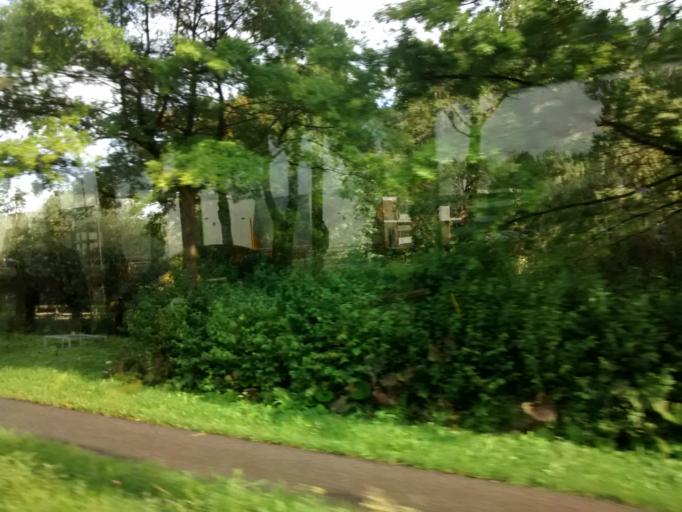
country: NL
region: South Holland
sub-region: Gemeente Gouda
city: Bloemendaal
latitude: 52.0219
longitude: 4.6870
